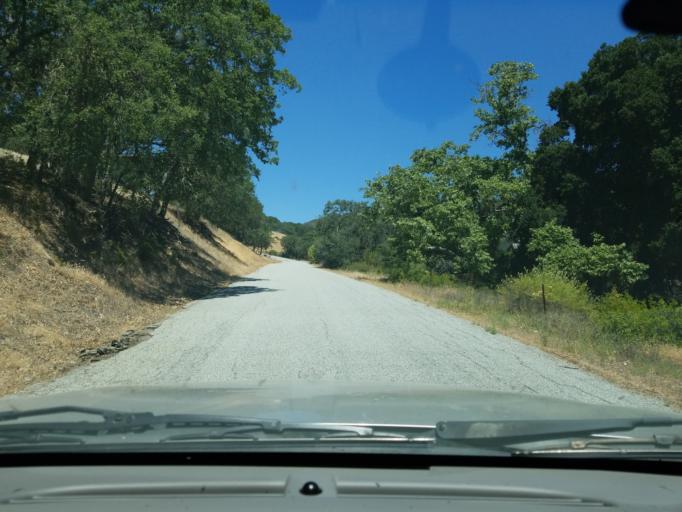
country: US
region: California
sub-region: Monterey County
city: Gonzales
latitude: 36.3391
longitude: -121.5004
